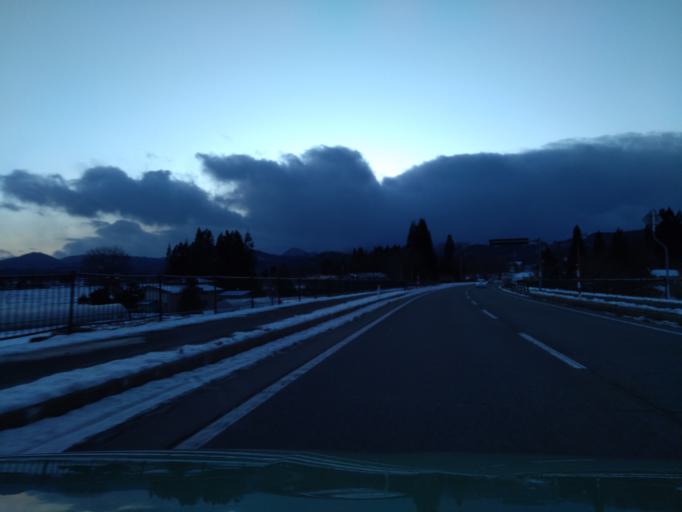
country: JP
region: Iwate
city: Shizukuishi
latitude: 39.6983
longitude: 140.9529
